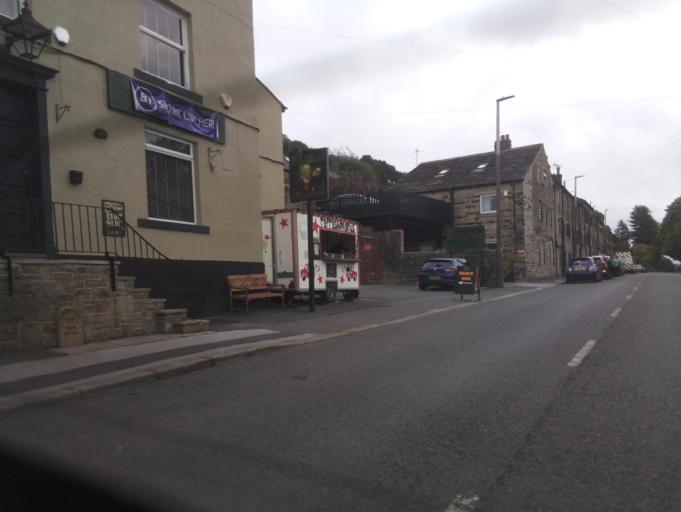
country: GB
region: England
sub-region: Kirklees
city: Holmfirth
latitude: 53.5611
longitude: -1.8101
